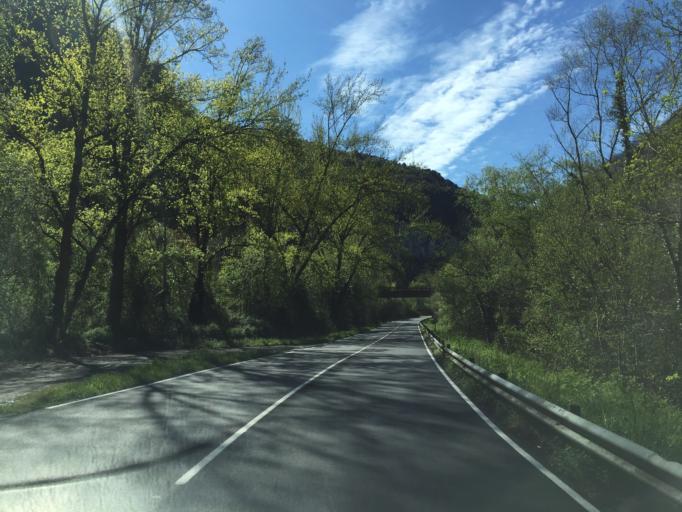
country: ES
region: Asturias
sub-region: Province of Asturias
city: Proaza
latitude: 43.3091
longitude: -5.9867
